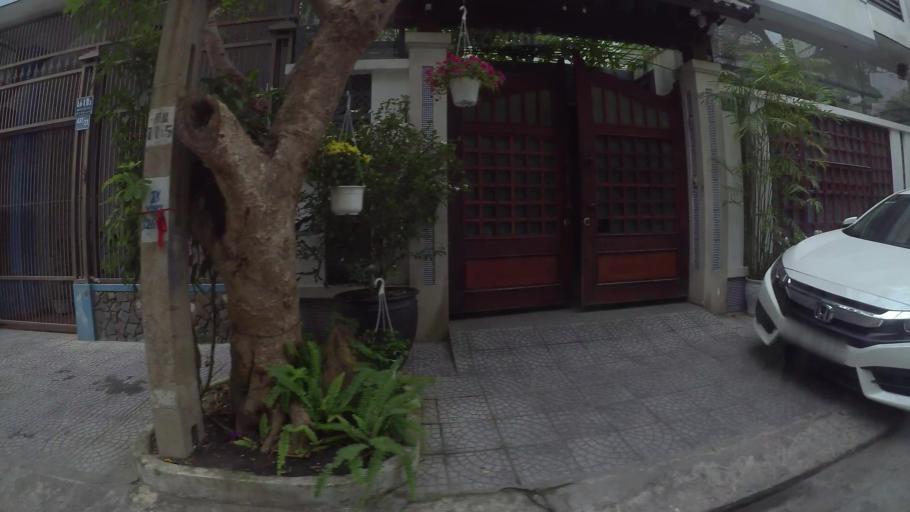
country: VN
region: Da Nang
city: Da Nang
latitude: 16.0795
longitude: 108.2144
